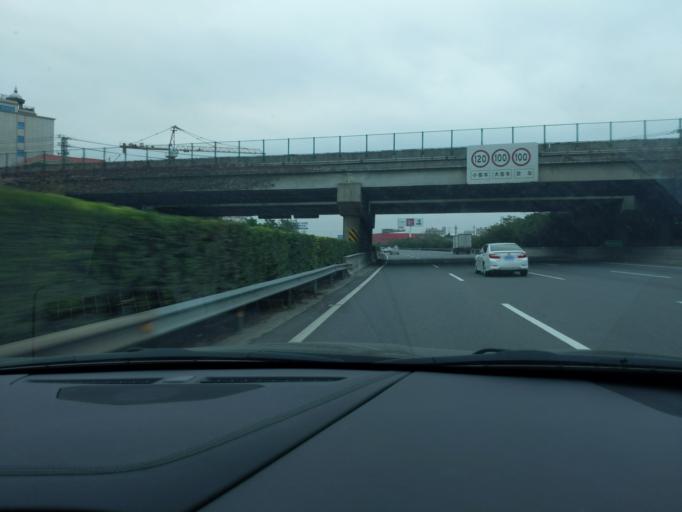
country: CN
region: Fujian
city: Neikeng
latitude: 24.7512
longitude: 118.4396
